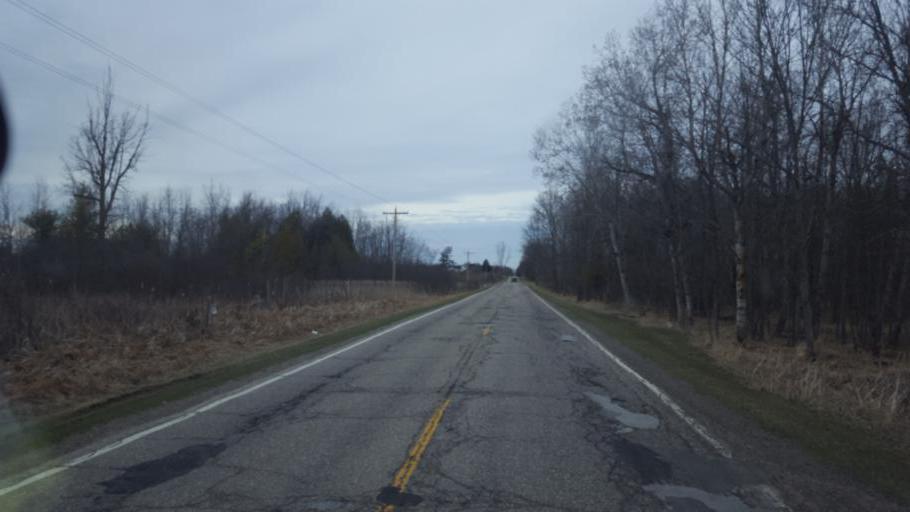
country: US
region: Michigan
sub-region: Montcalm County
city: Edmore
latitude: 43.4802
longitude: -85.0053
